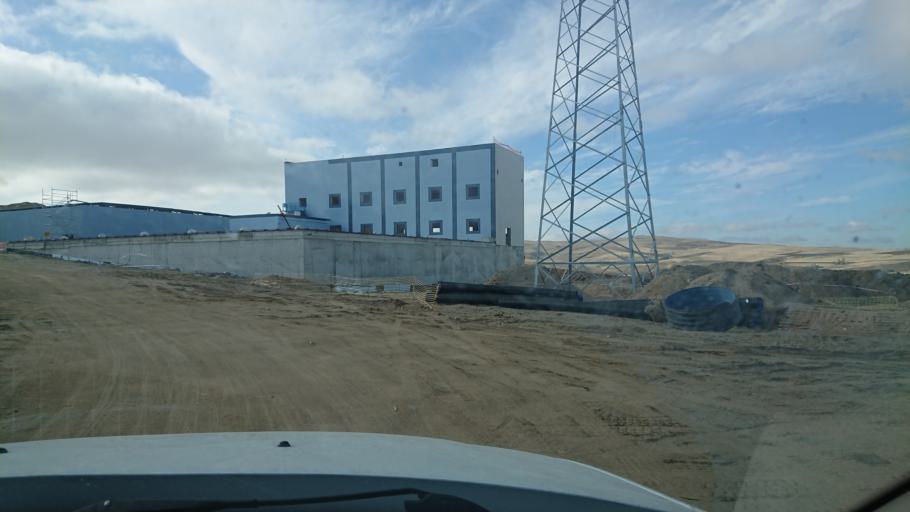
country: TR
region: Aksaray
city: Agacoren
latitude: 38.8466
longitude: 33.9446
